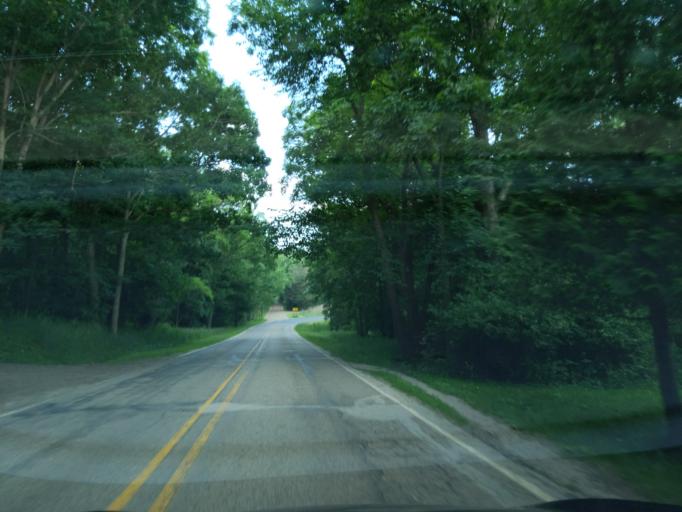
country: US
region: Michigan
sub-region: Ingham County
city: Haslett
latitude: 42.8152
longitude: -84.3741
